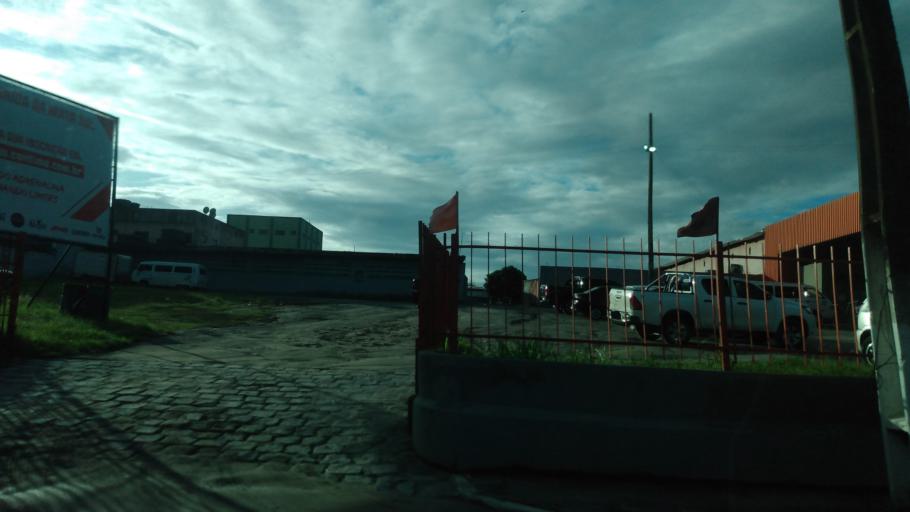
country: BR
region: Pernambuco
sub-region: Palmares
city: Palmares
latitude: -8.6799
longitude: -35.5804
